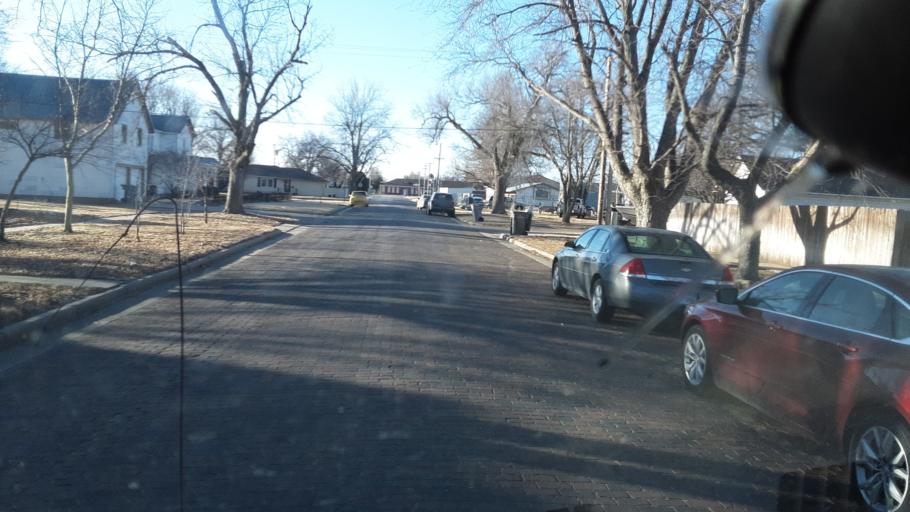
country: US
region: Kansas
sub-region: Barton County
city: Ellinwood
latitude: 38.3555
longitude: -98.5793
